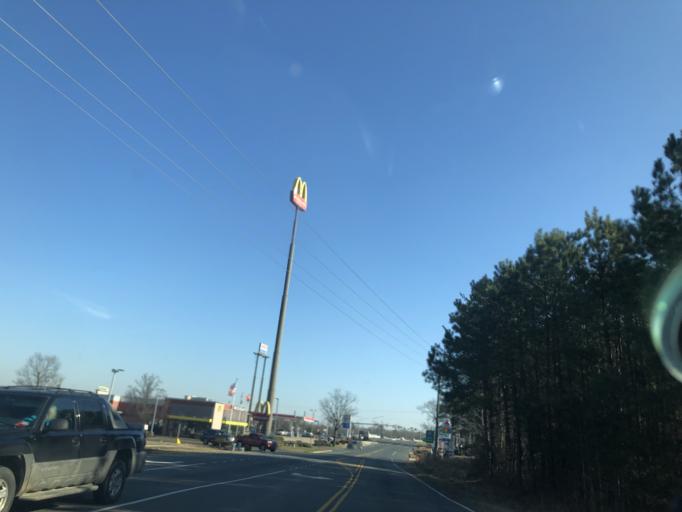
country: US
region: Virginia
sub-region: Spotsylvania County
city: Spotsylvania Courthouse
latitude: 38.1323
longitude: -77.5153
